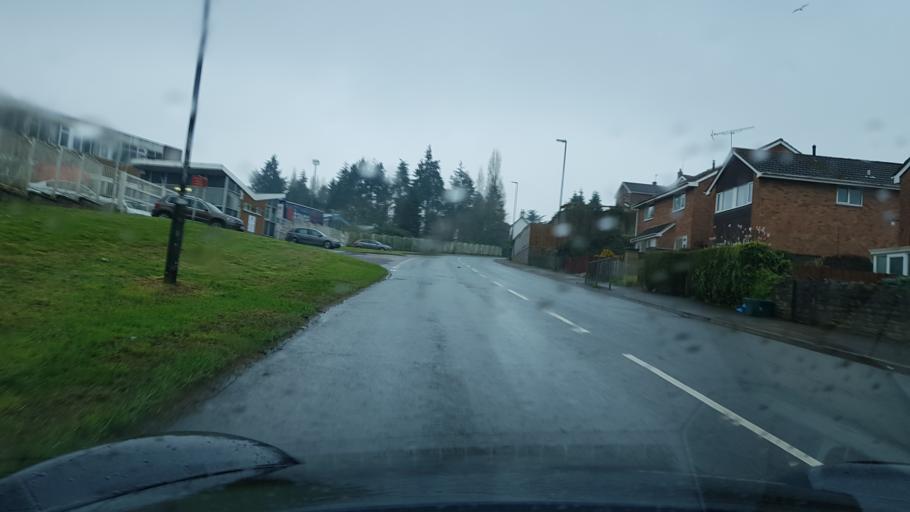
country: GB
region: England
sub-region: Gloucestershire
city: Mitcheldean
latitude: 51.8692
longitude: -2.4880
